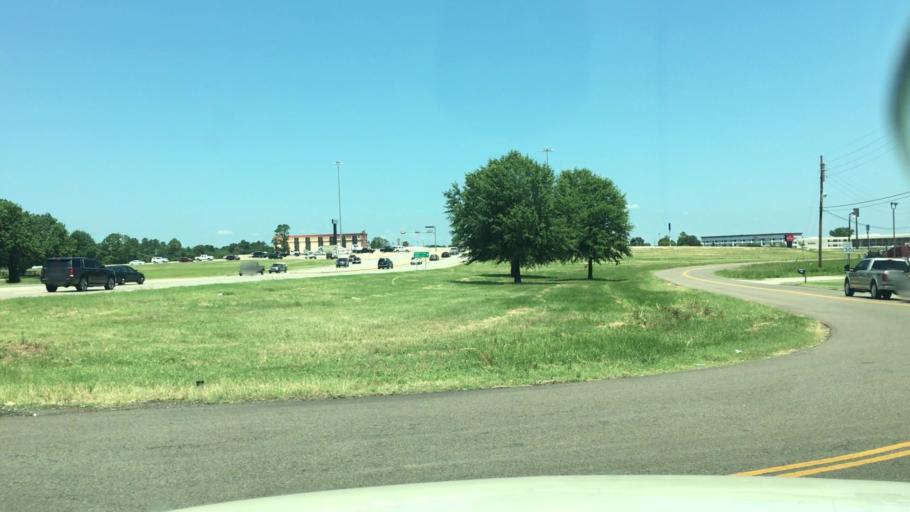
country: US
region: Arkansas
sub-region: Miller County
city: Texarkana
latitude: 33.4670
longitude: -94.0426
